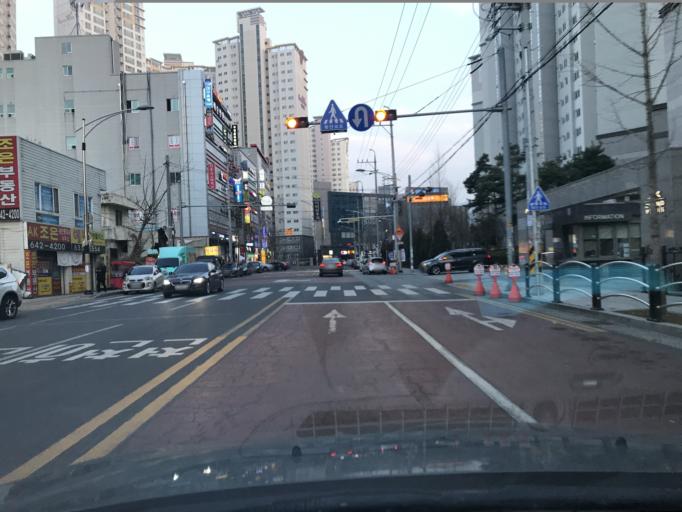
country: KR
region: Daegu
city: Hwawon
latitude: 35.8159
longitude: 128.5193
